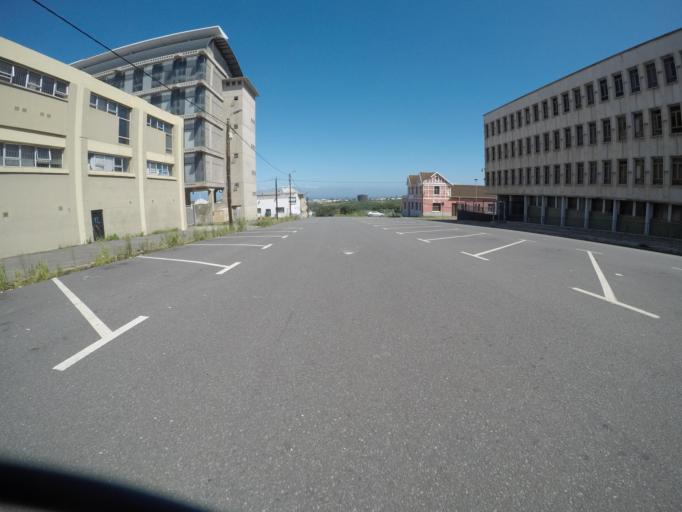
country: ZA
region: Eastern Cape
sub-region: Buffalo City Metropolitan Municipality
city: East London
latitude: -33.0209
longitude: 27.9044
